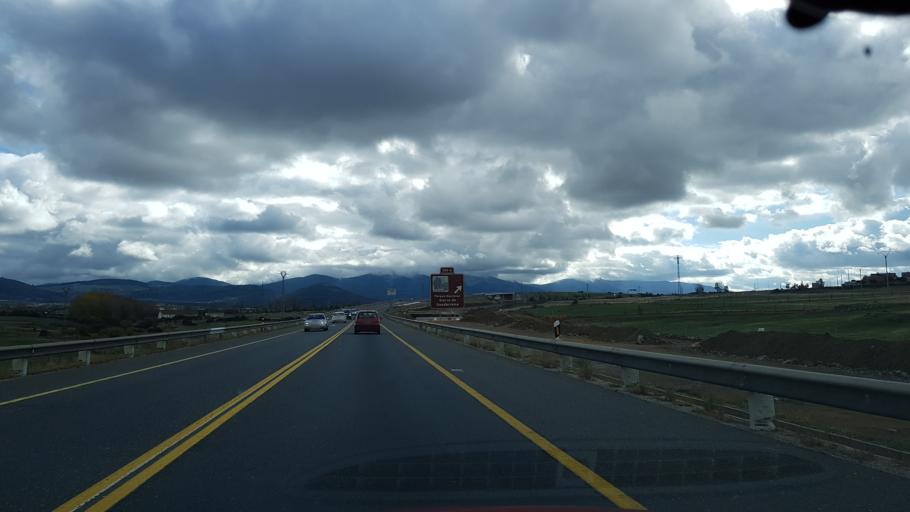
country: ES
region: Castille and Leon
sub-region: Provincia de Segovia
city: San Cristobal de Segovia
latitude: 40.9342
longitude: -4.0854
